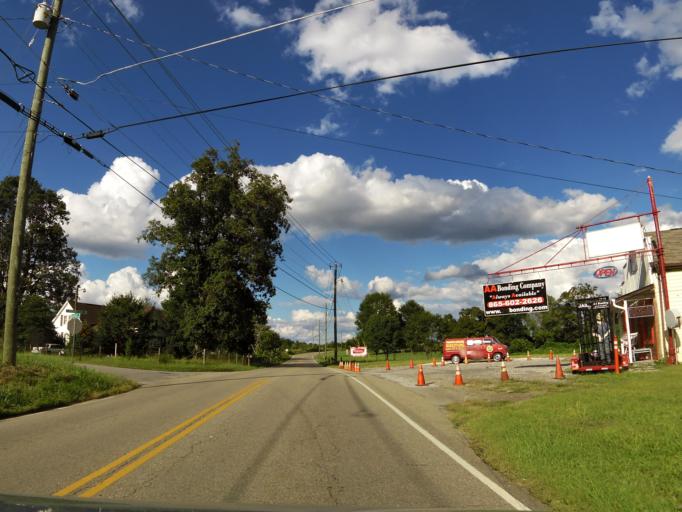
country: US
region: Tennessee
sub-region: Knox County
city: Knoxville
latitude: 36.0572
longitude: -83.8674
